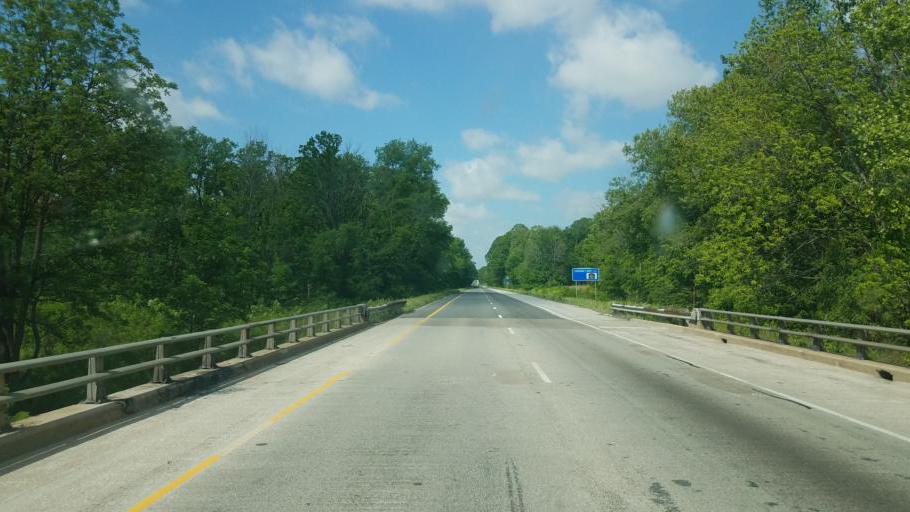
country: US
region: Indiana
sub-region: Clay County
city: Brazil
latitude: 39.4583
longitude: -87.0894
